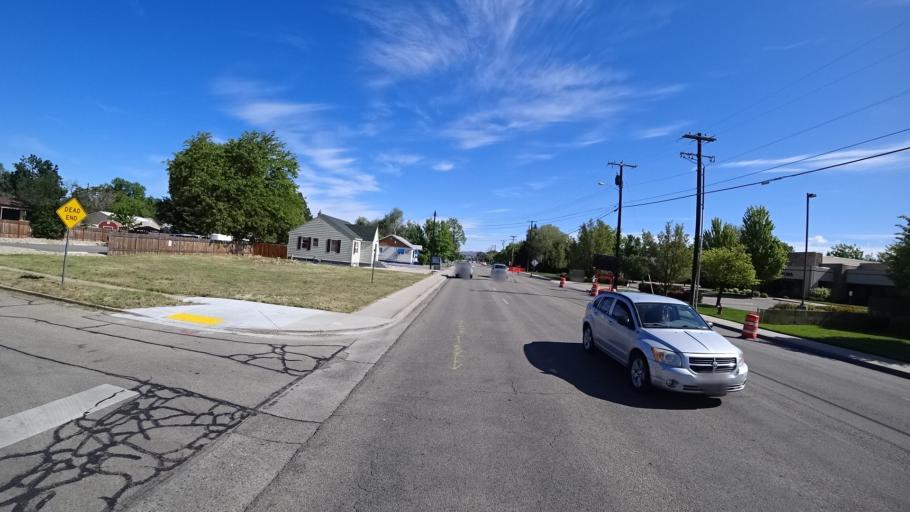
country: US
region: Idaho
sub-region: Ada County
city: Garden City
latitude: 43.5993
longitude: -116.2436
